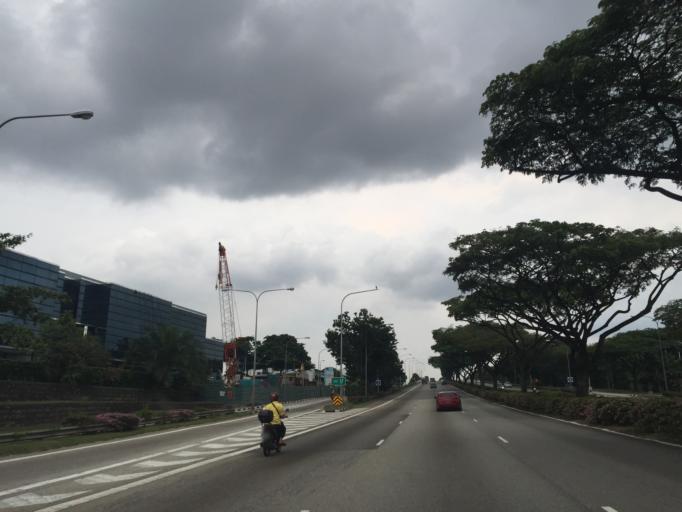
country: SG
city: Singapore
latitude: 1.3220
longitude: 103.7044
